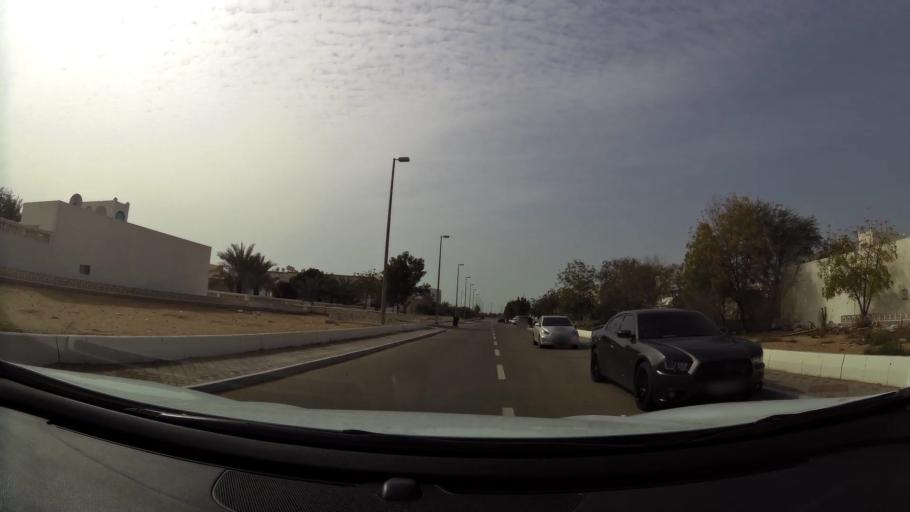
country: AE
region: Abu Dhabi
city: Abu Dhabi
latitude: 24.6036
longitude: 54.7022
